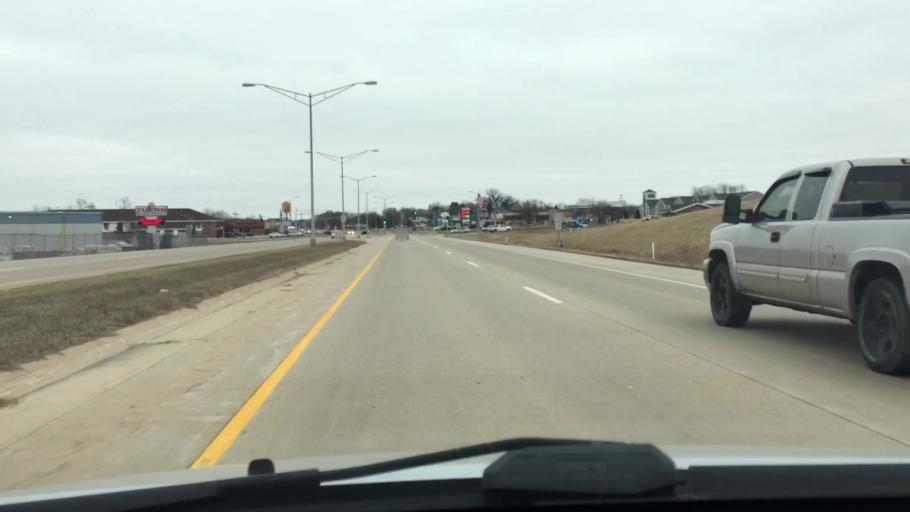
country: US
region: Wisconsin
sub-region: Jefferson County
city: Watertown
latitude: 43.1681
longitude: -88.7334
